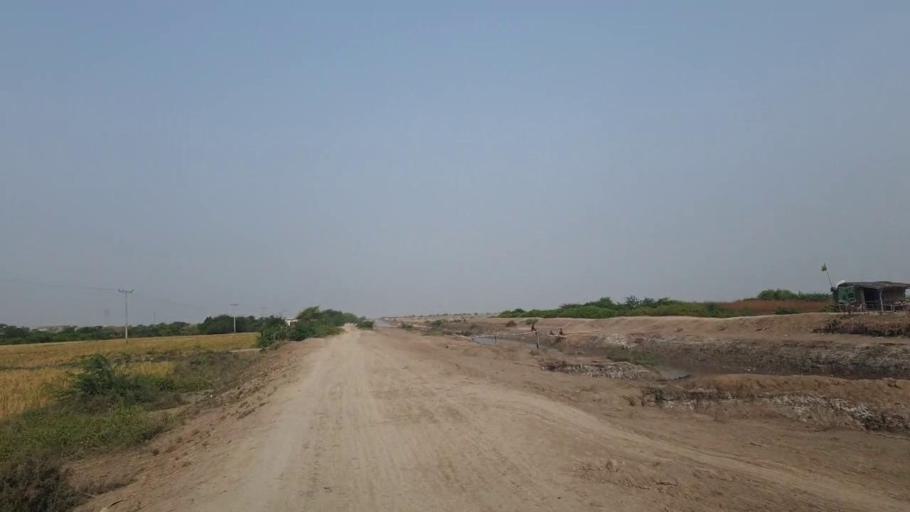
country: PK
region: Sindh
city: Badin
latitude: 24.7146
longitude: 68.7721
